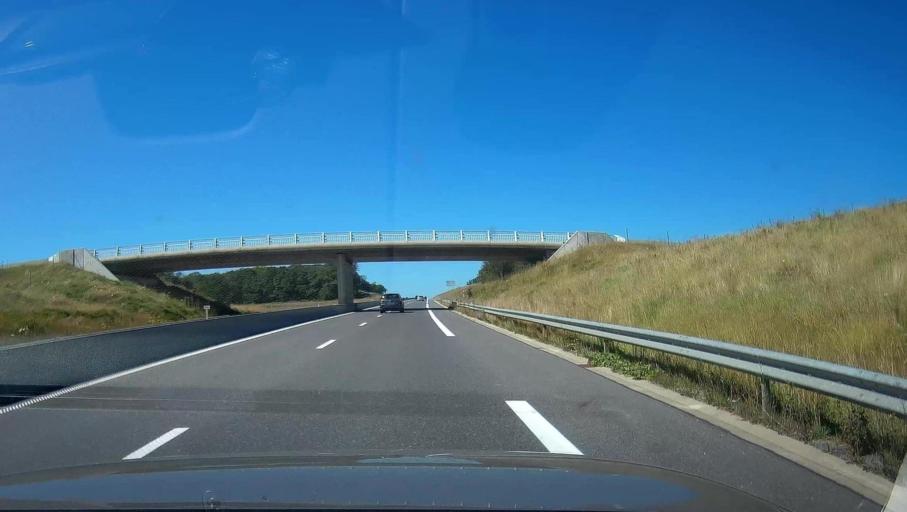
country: FR
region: Champagne-Ardenne
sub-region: Departement des Ardennes
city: Warcq
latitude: 49.7528
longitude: 4.6598
